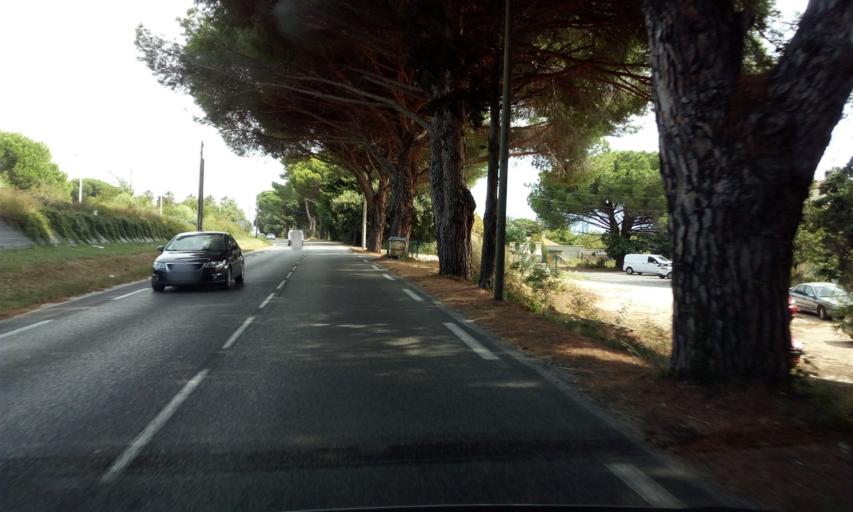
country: FR
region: Provence-Alpes-Cote d'Azur
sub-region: Departement du Var
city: Bormes-les-Mimosas
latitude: 43.1439
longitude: 6.3267
